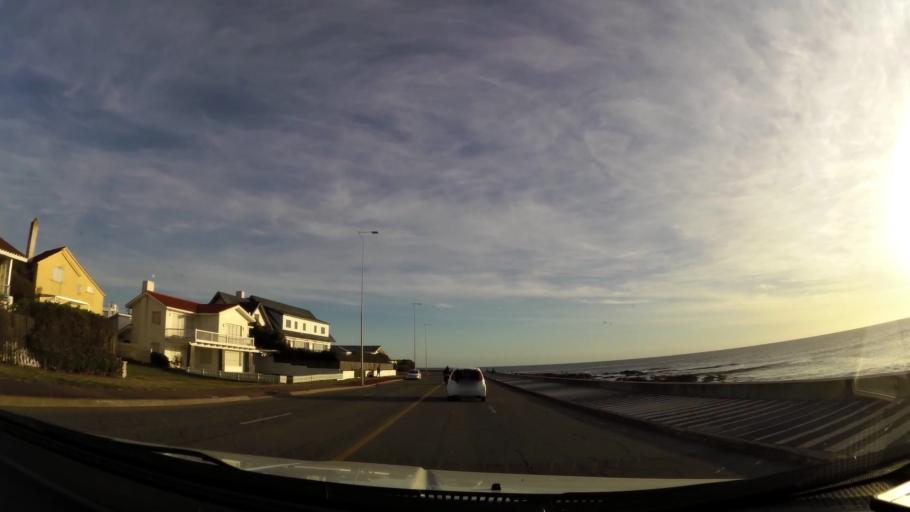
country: UY
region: Maldonado
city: Punta del Este
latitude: -34.9708
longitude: -54.9538
